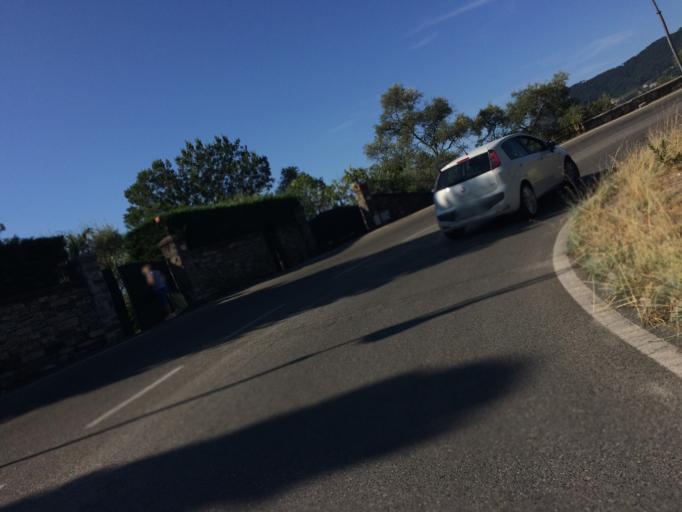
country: IT
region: Liguria
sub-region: Provincia di Genova
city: Rapallo
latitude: 44.3432
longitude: 9.2268
